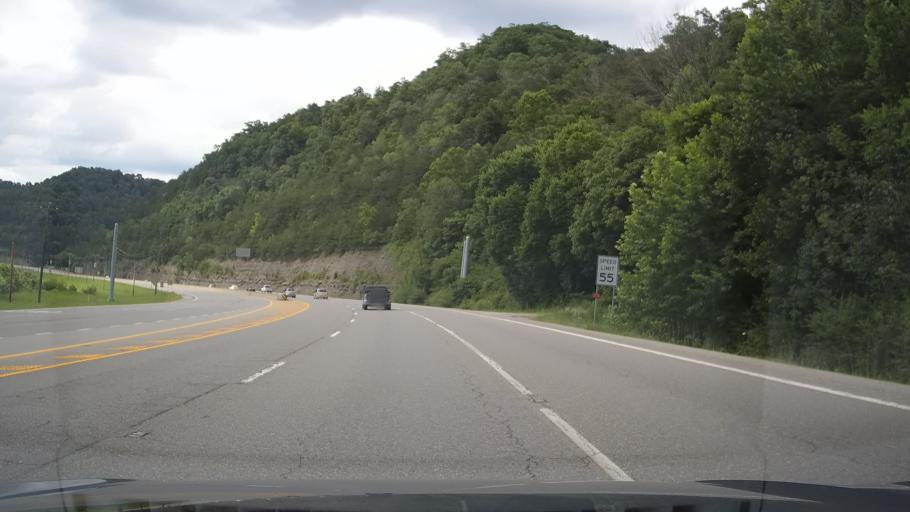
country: US
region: Kentucky
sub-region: Pike County
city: Coal Run Village
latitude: 37.5056
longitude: -82.5326
